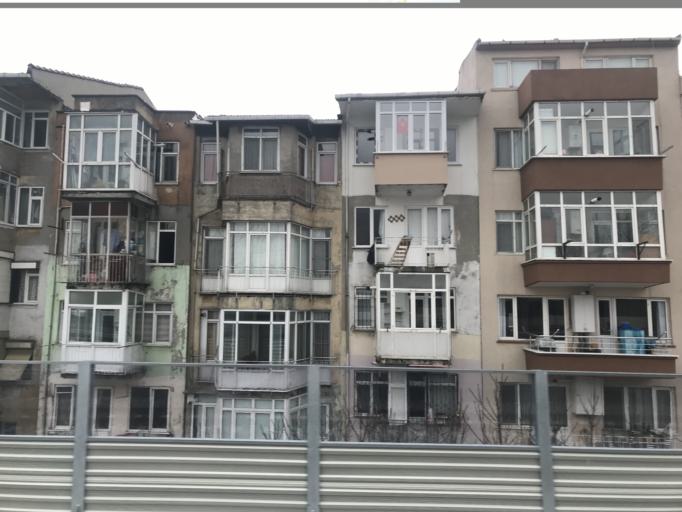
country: TR
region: Istanbul
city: Zeytinburnu
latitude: 40.9819
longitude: 28.8828
